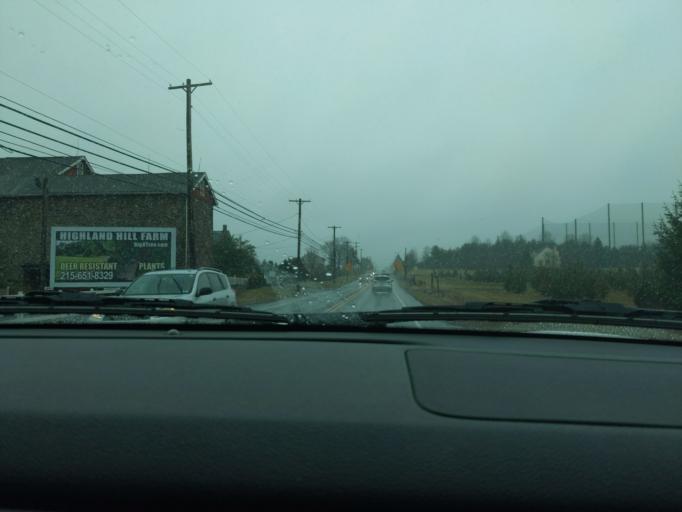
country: US
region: Pennsylvania
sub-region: Bucks County
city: Plumsteadville
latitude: 40.3469
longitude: -75.1605
